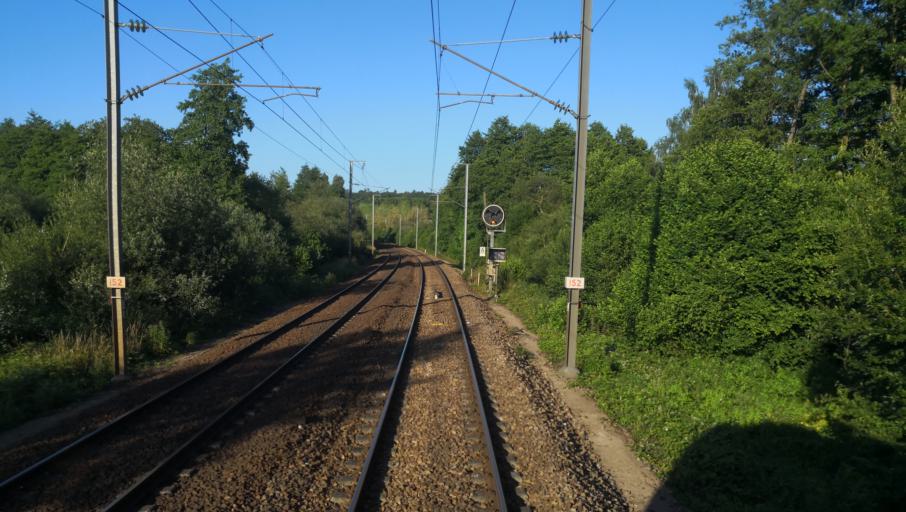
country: FR
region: Haute-Normandie
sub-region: Departement de l'Eure
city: Serquigny
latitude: 49.0916
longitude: 0.6843
